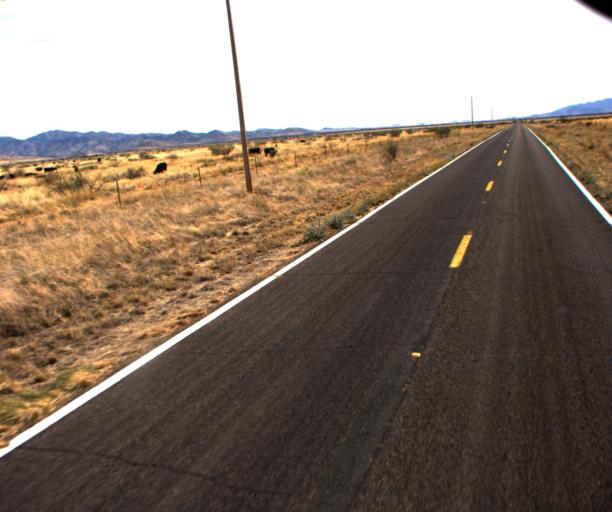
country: US
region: Arizona
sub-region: Cochise County
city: Willcox
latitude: 31.9307
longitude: -109.4914
